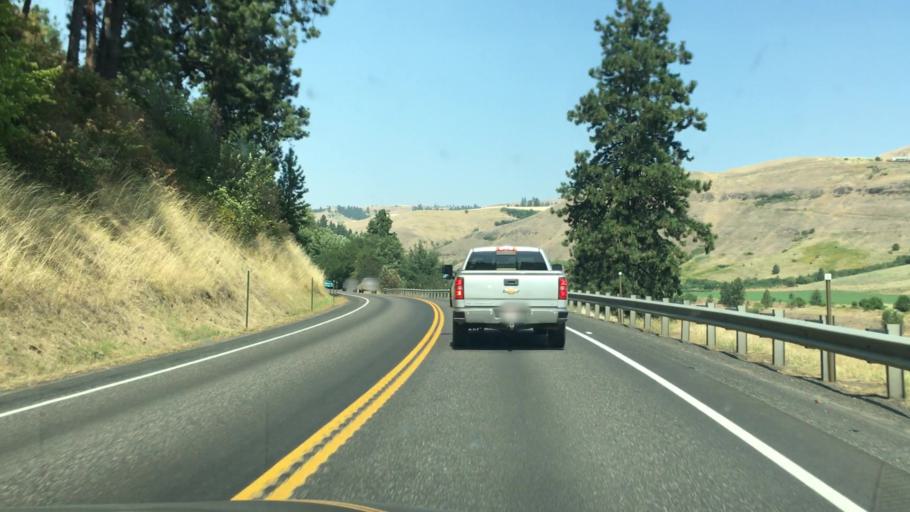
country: US
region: Idaho
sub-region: Clearwater County
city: Orofino
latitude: 46.5012
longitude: -116.5020
